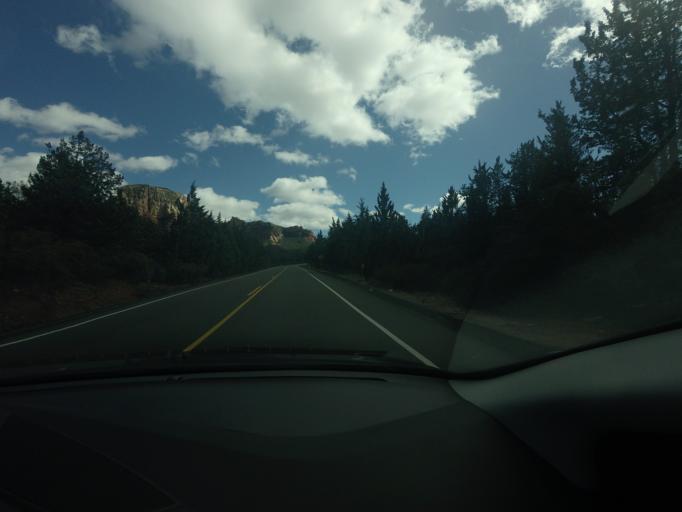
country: US
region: Arizona
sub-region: Yavapai County
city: West Sedona
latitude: 34.8957
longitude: -111.8262
